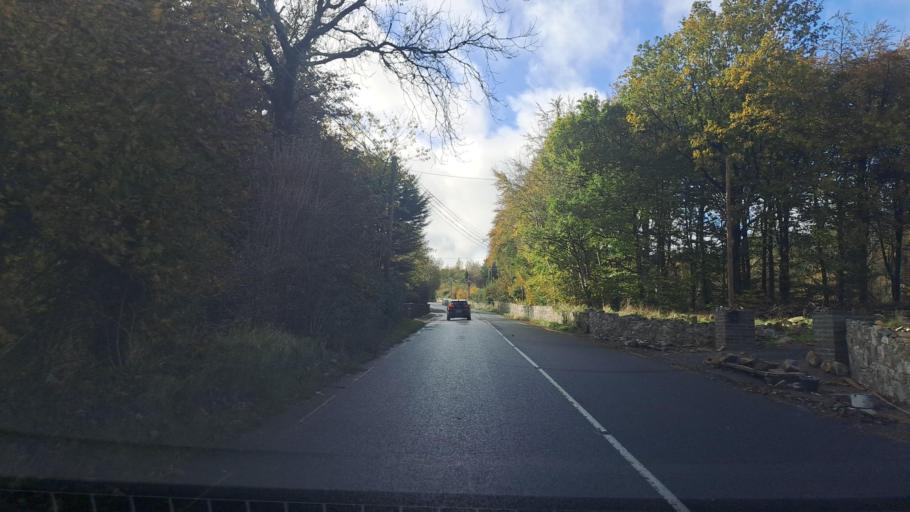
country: IE
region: Ulster
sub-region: County Monaghan
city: Monaghan
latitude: 54.2203
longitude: -6.9792
